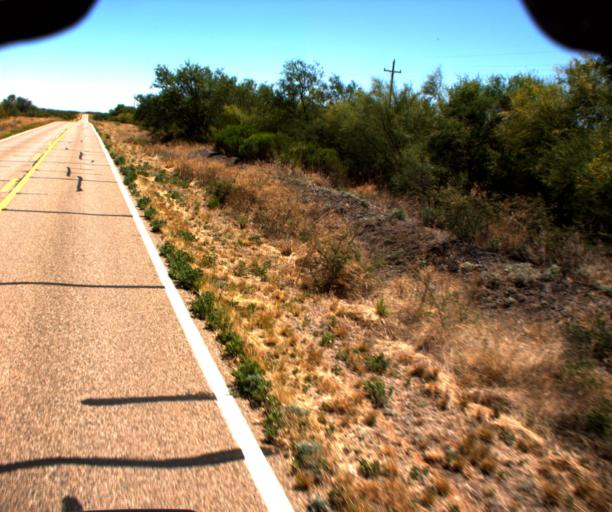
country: US
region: Arizona
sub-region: Pima County
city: Three Points
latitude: 31.7206
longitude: -111.4879
